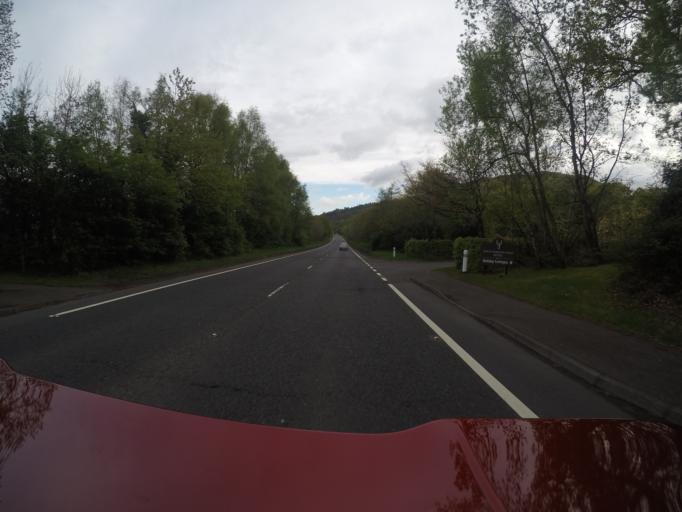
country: GB
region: Scotland
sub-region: West Dunbartonshire
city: Balloch
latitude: 56.1002
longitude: -4.6426
